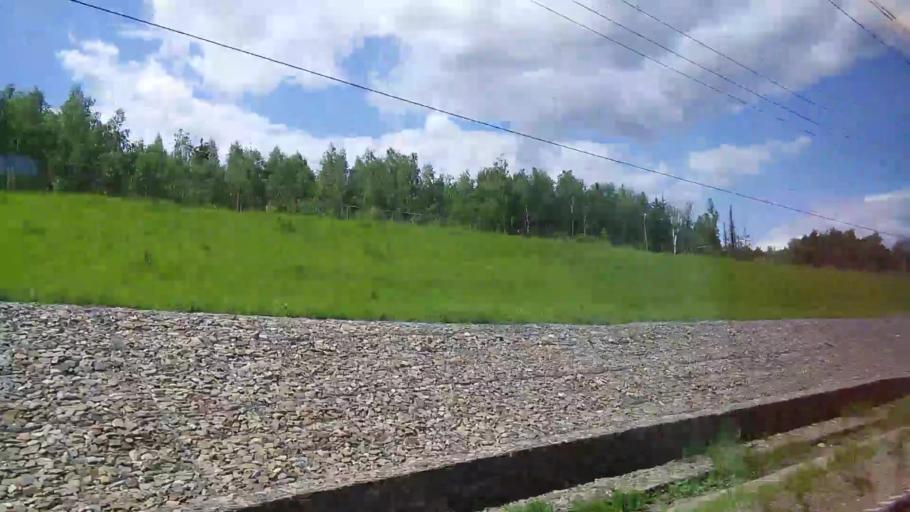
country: RU
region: Moskovskaya
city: Sheremet'yevskiy
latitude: 55.9831
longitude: 37.4683
